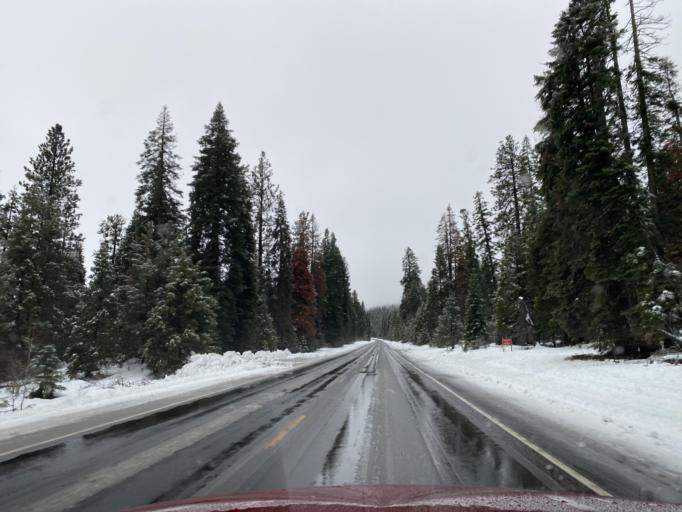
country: US
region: Oregon
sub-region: Klamath County
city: Klamath Falls
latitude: 42.5452
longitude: -122.0875
